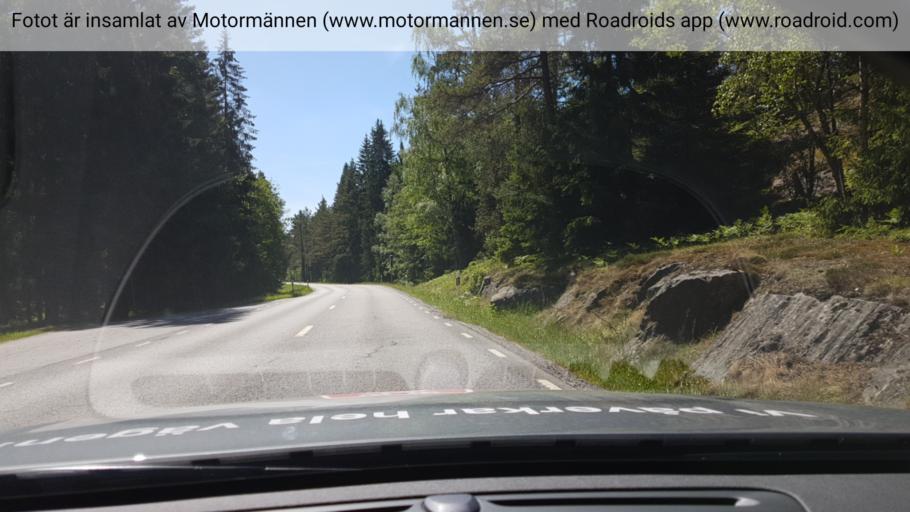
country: SE
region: Stockholm
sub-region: Haninge Kommun
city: Haninge
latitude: 59.1509
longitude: 18.1794
